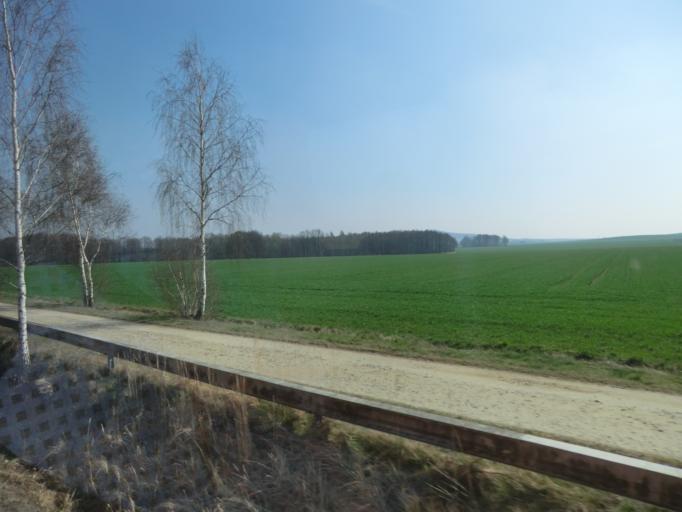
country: DE
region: Saxony
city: Markersdorf
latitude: 51.1252
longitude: 14.8632
